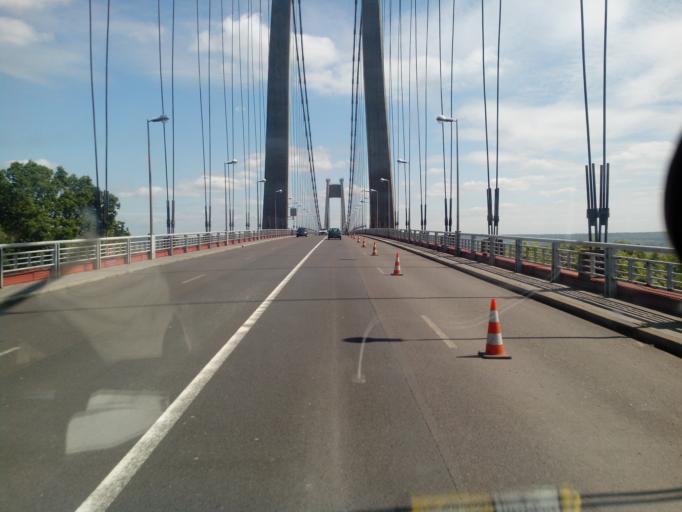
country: FR
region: Haute-Normandie
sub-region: Departement de la Seine-Maritime
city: Tancarville
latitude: 49.4760
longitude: 0.4615
